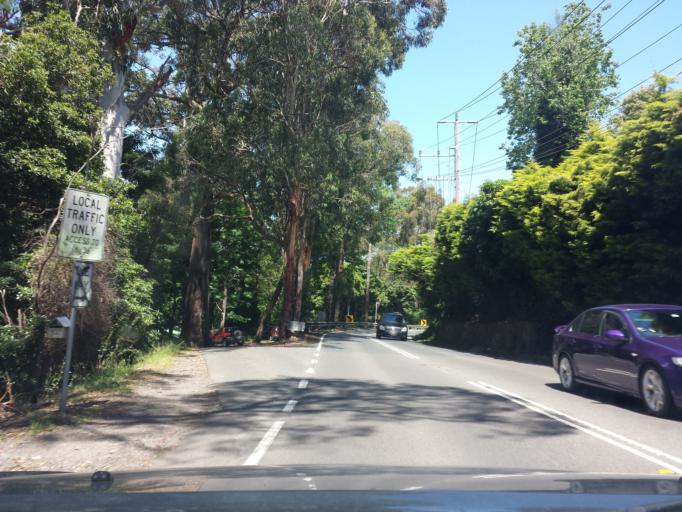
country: AU
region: Victoria
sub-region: Yarra Ranges
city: Belgrave Heights
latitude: -37.9134
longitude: 145.3562
